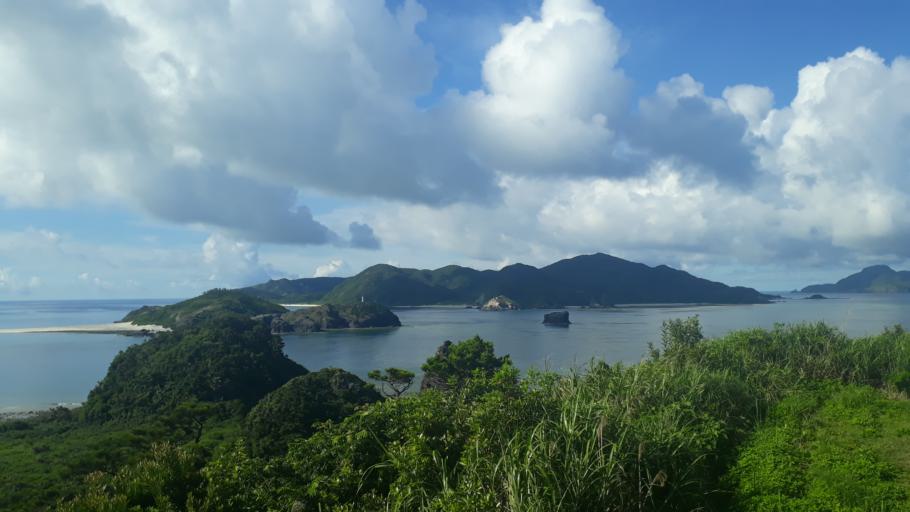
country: JP
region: Okinawa
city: Naha-shi
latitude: 26.2283
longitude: 127.2831
